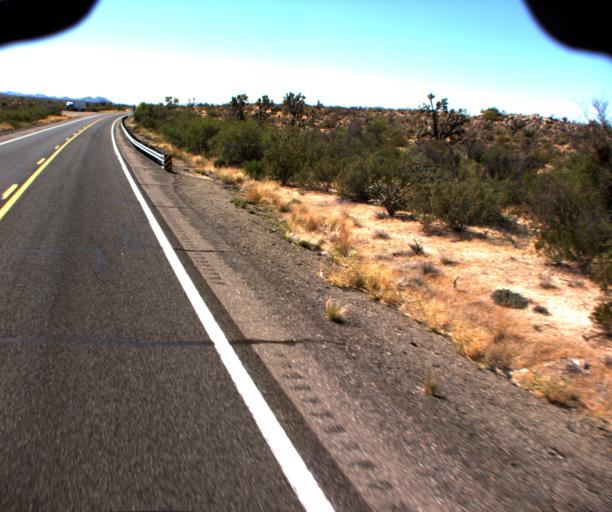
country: US
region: Arizona
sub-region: Yavapai County
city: Congress
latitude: 34.2332
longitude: -113.0718
